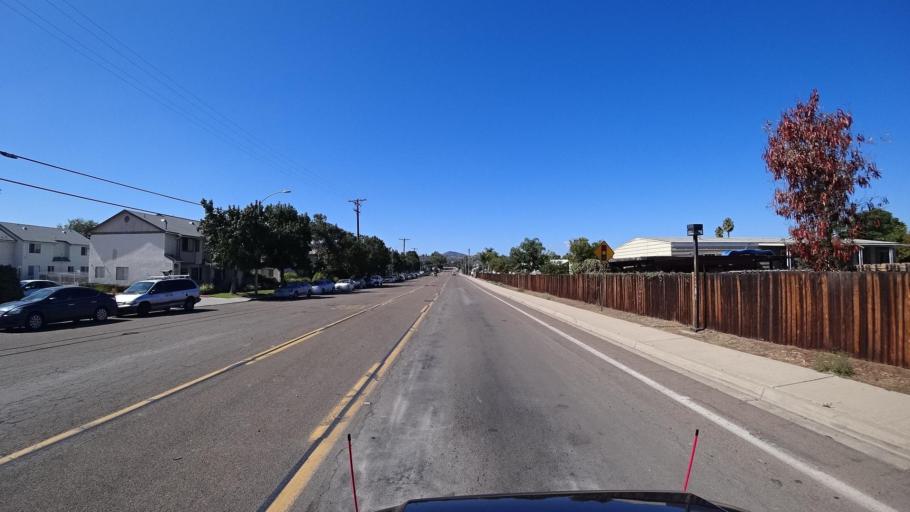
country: US
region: California
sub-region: San Diego County
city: El Cajon
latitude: 32.8134
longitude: -116.9562
